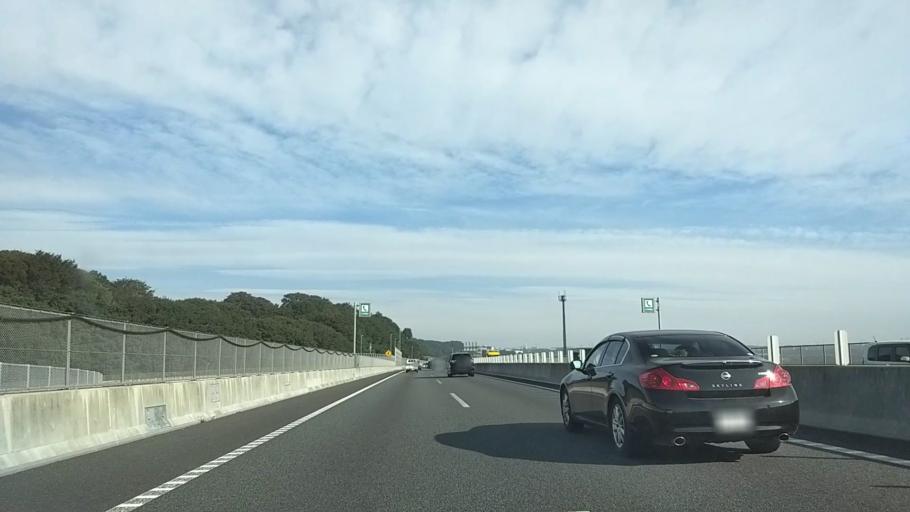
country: JP
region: Kanagawa
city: Zama
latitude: 35.4886
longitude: 139.3696
